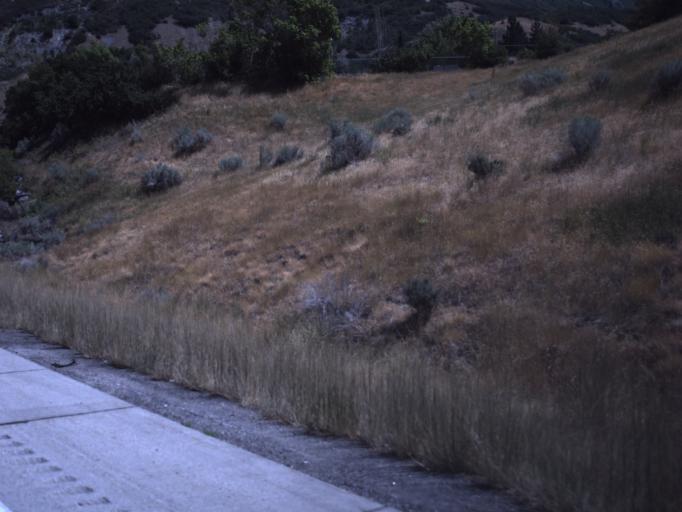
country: US
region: Utah
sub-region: Utah County
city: Orem
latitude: 40.3285
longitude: -111.6270
